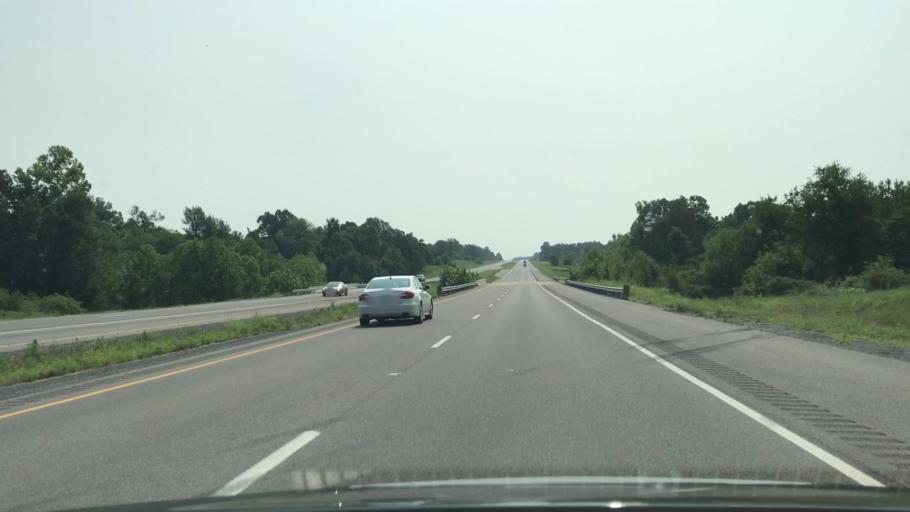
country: US
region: Kentucky
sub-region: Graves County
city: Mayfield
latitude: 36.6690
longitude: -88.4970
